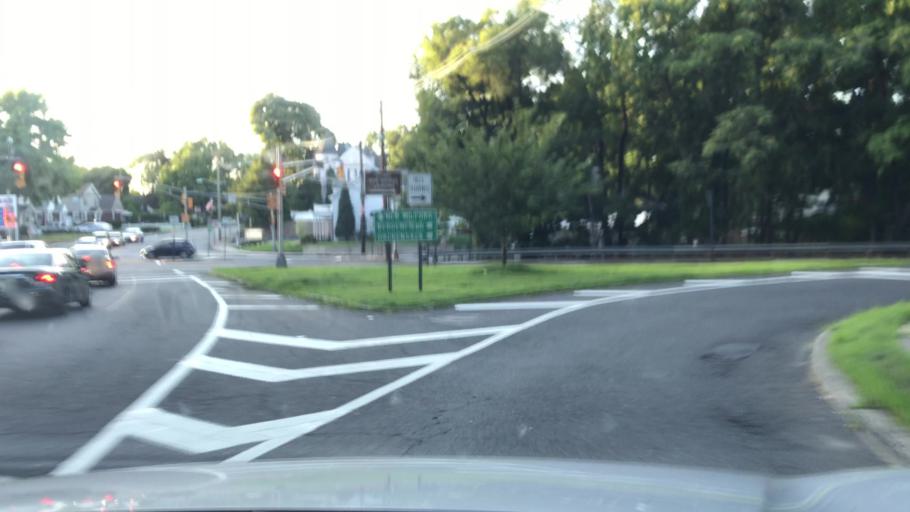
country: US
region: New Jersey
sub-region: Bergen County
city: River Edge
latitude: 40.9156
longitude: -74.0248
